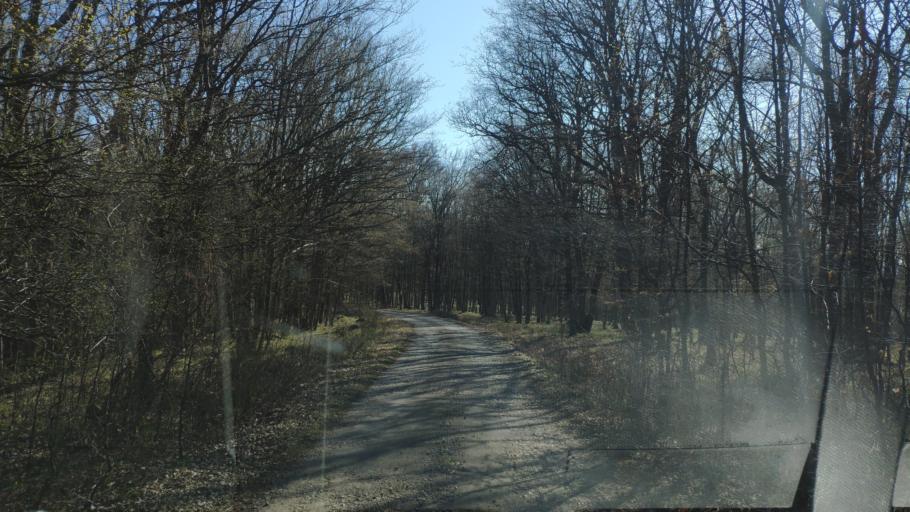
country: SK
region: Kosicky
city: Roznava
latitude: 48.5904
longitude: 20.4085
